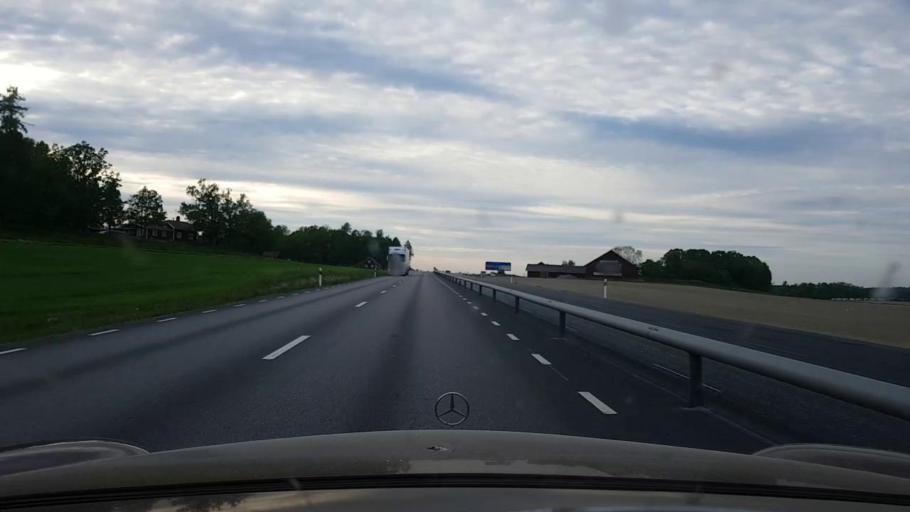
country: SE
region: OErebro
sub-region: Askersunds Kommun
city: Askersund
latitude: 58.8608
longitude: 14.9035
